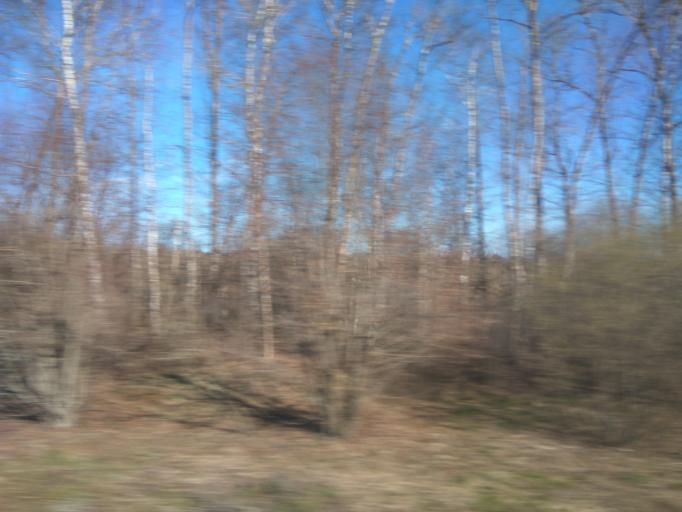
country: RU
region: Pskov
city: Izborsk
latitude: 57.7191
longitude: 27.9285
